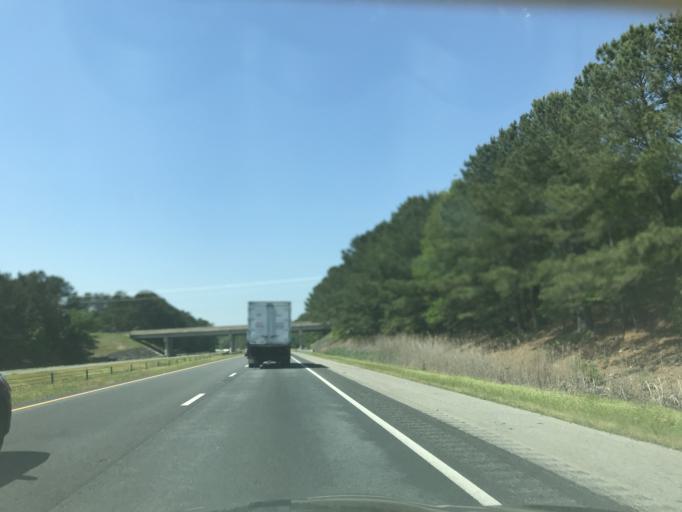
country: US
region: North Carolina
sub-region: Johnston County
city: Benson
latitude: 35.3748
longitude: -78.5030
